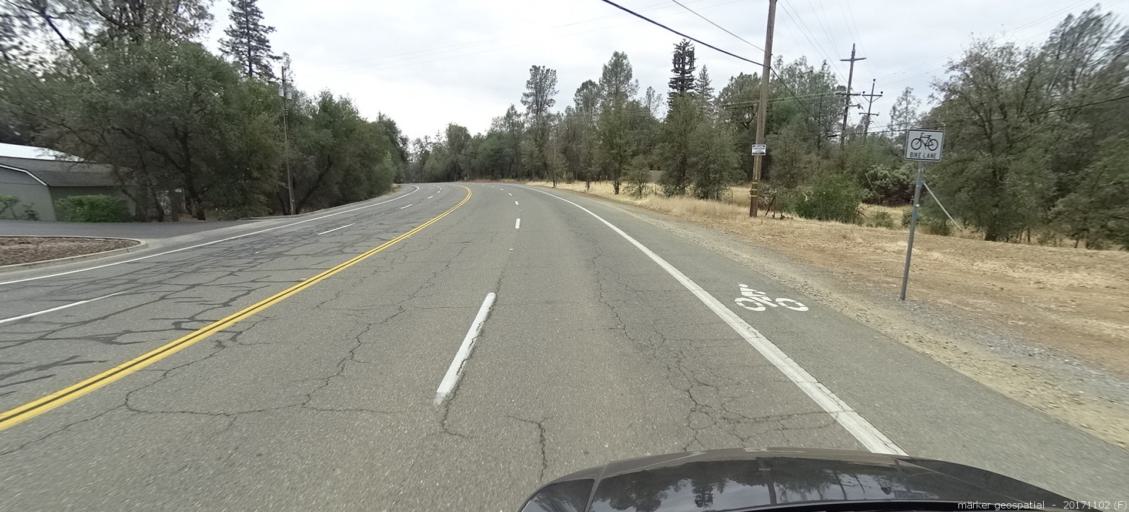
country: US
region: California
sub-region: Shasta County
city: Central Valley (historical)
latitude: 40.6481
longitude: -122.3979
